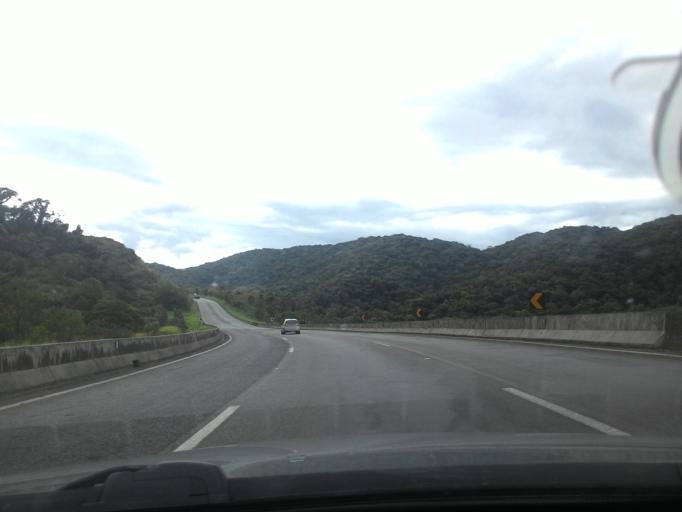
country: BR
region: Sao Paulo
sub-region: Cajati
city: Cajati
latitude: -24.9470
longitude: -48.4250
